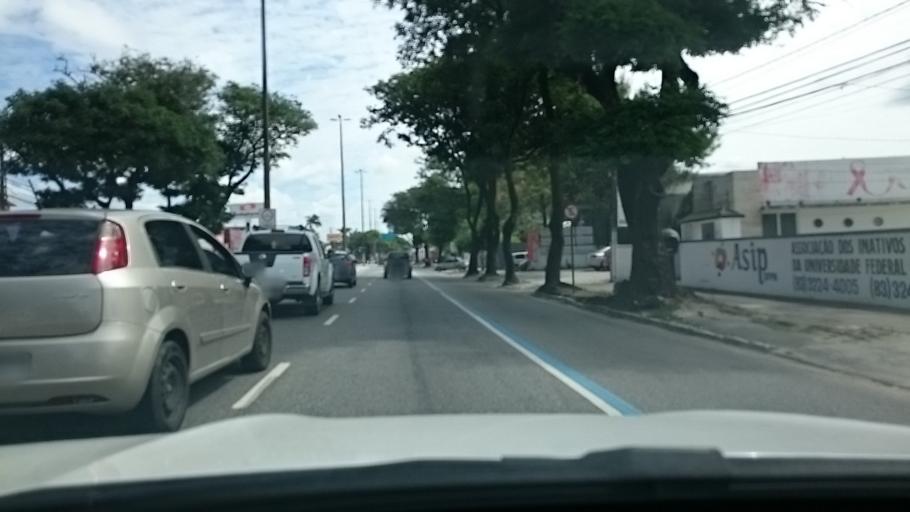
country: BR
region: Paraiba
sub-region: Joao Pessoa
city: Joao Pessoa
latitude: -7.1197
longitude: -34.8648
